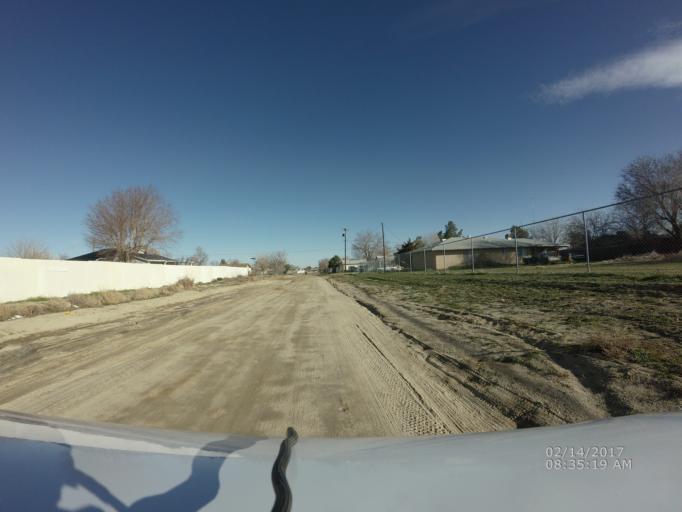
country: US
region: California
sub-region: Los Angeles County
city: Littlerock
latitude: 34.5533
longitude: -117.9450
